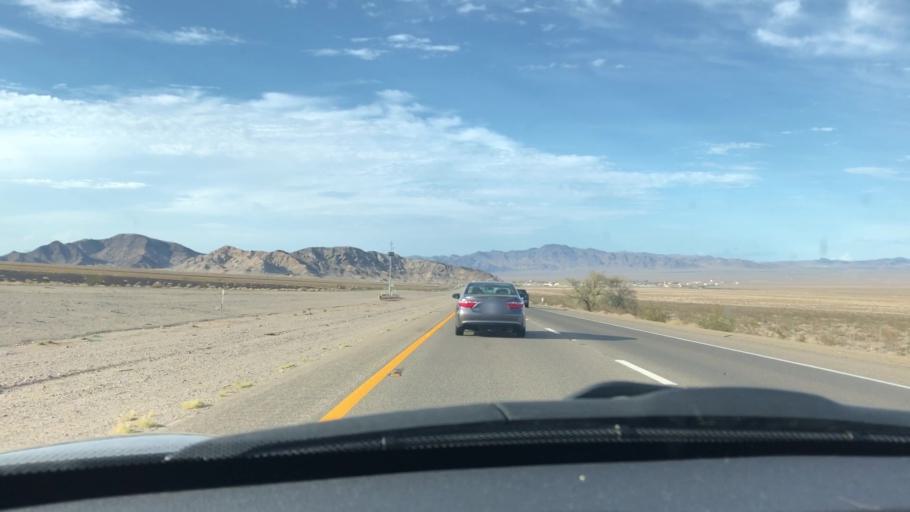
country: US
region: California
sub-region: San Bernardino County
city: Fort Irwin
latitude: 35.2316
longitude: -116.1019
